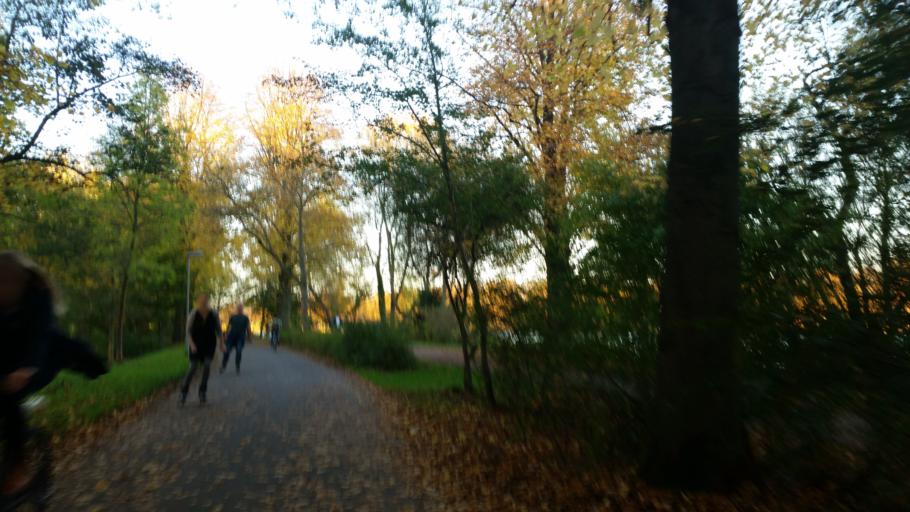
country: DE
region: Lower Saxony
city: Hannover
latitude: 52.3496
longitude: 9.7455
